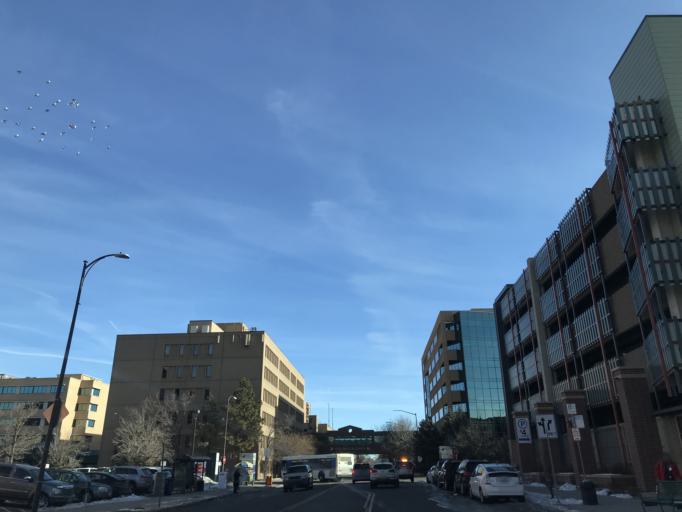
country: US
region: Colorado
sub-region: Arapahoe County
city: Glendale
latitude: 39.7310
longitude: -104.9360
